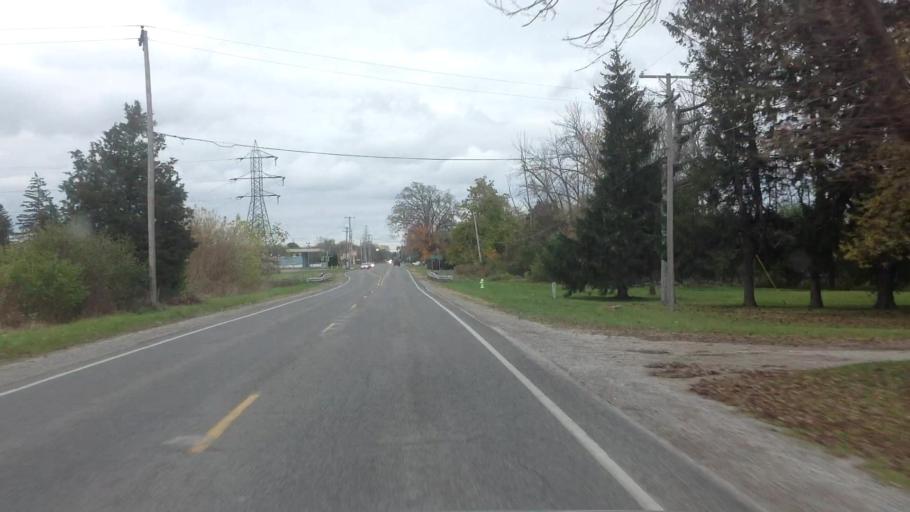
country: US
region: Michigan
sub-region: Saginaw County
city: Bridgeport
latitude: 43.3803
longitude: -83.9188
